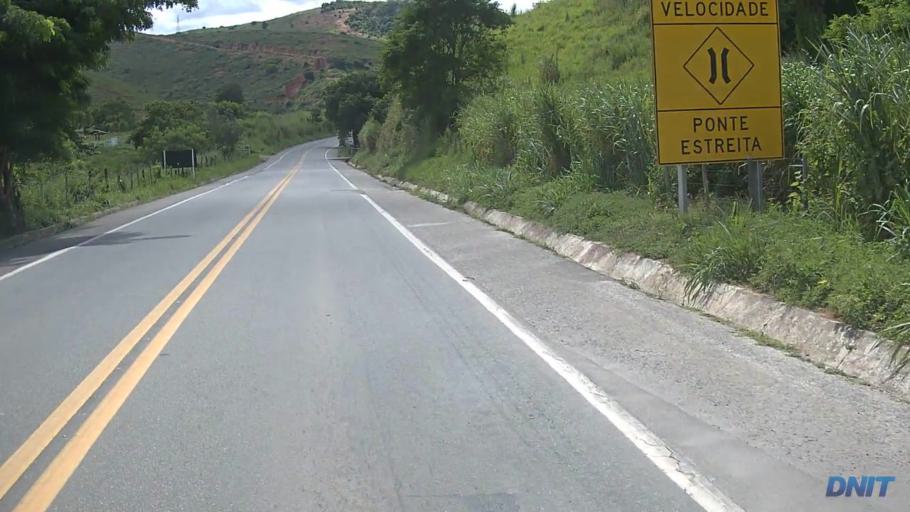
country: BR
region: Minas Gerais
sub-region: Governador Valadares
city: Governador Valadares
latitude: -18.9533
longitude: -42.0724
